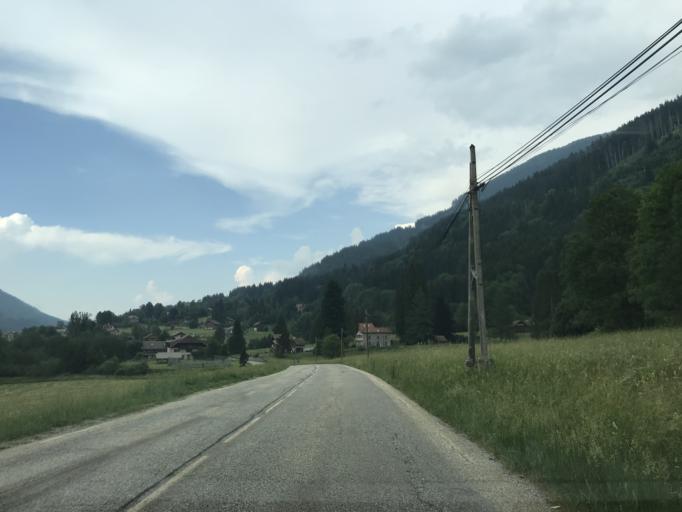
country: FR
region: Rhone-Alpes
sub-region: Departement de l'Isere
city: Theys
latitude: 45.2996
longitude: 6.0800
